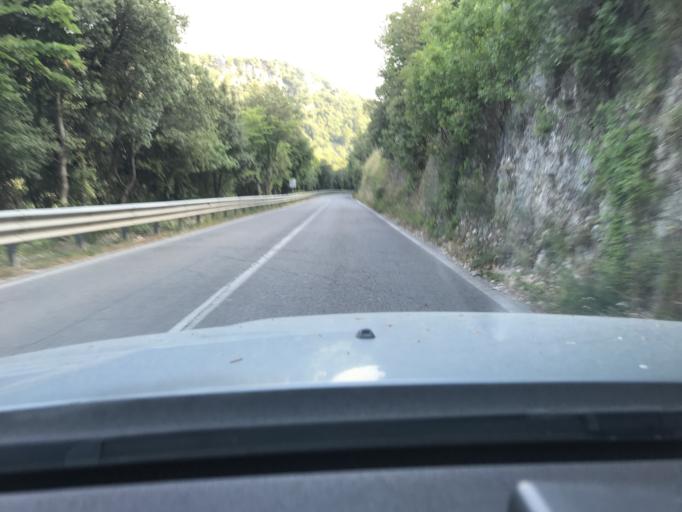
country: IT
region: Umbria
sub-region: Provincia di Terni
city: Amelia
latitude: 42.5572
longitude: 12.4090
